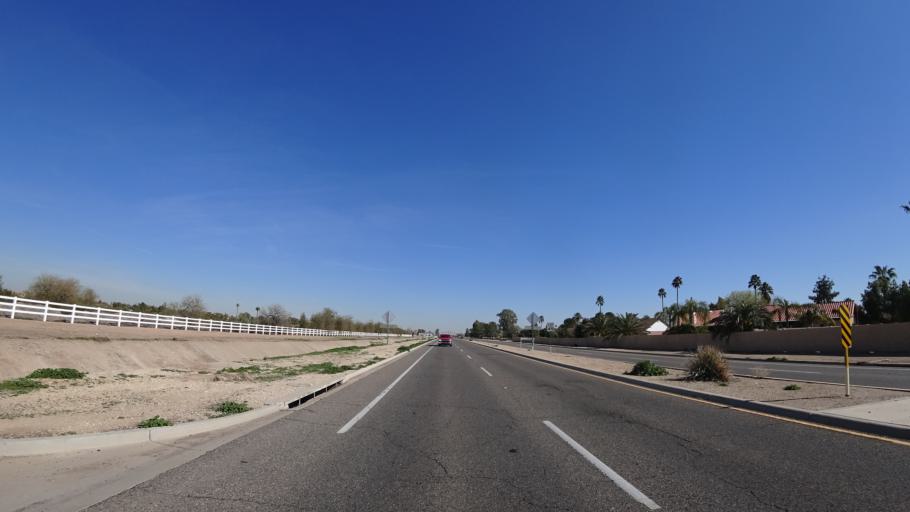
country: US
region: Arizona
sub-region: Maricopa County
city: Litchfield Park
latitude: 33.5081
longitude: -112.3467
